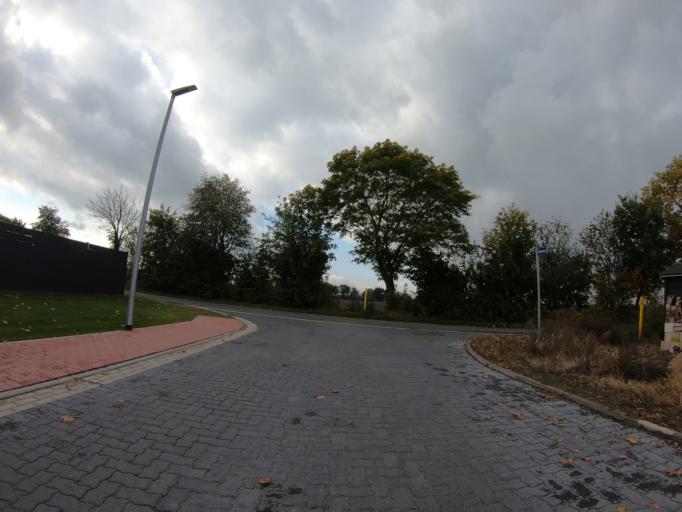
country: DE
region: Lower Saxony
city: Wahrenholz
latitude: 52.6177
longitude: 10.5918
